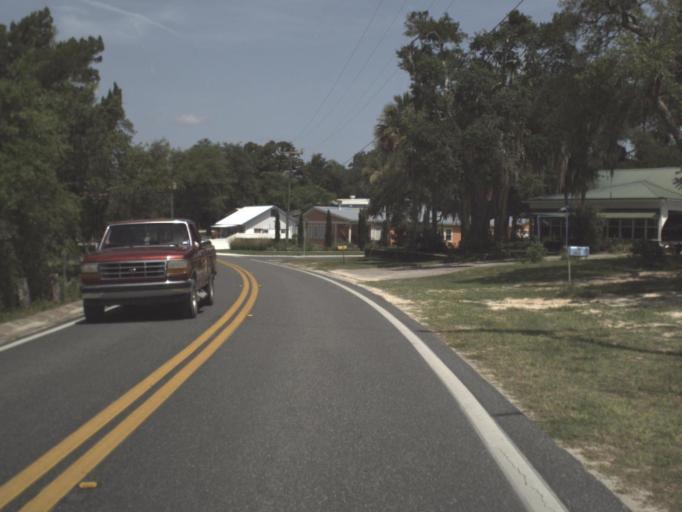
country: US
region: Florida
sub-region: Taylor County
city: Steinhatchee
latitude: 29.6692
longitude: -83.3792
